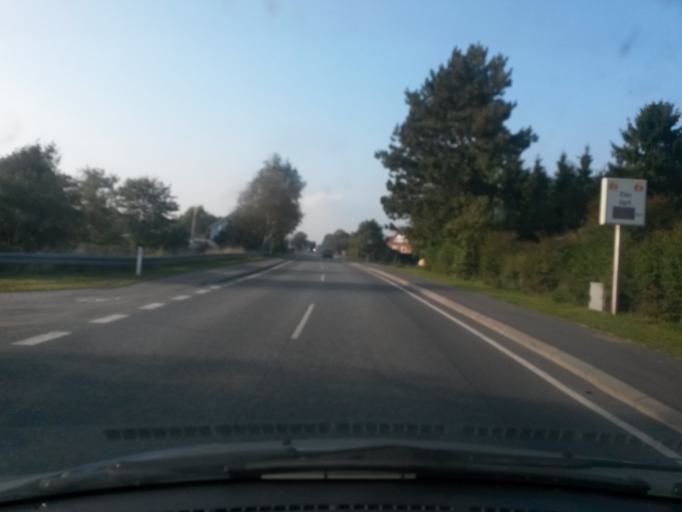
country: DK
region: Central Jutland
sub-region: Syddjurs Kommune
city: Hornslet
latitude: 56.3562
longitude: 10.3424
